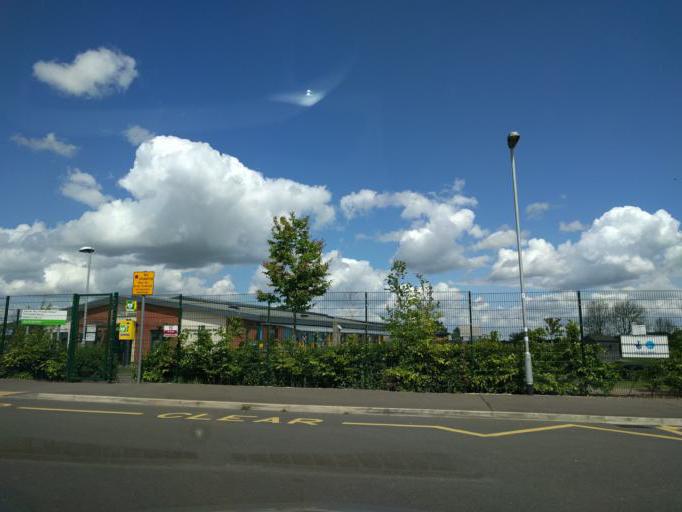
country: GB
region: England
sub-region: Nottinghamshire
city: Newark on Trent
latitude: 53.0503
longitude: -0.7681
